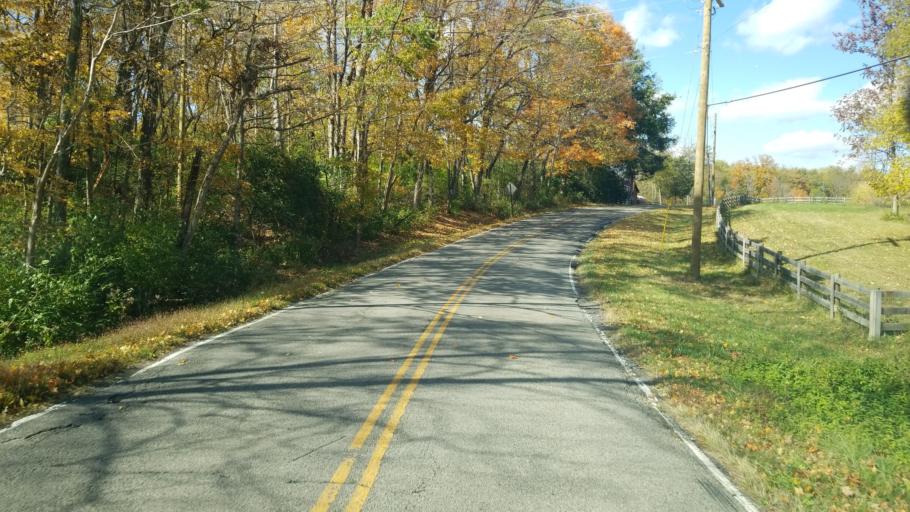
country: US
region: Ohio
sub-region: Warren County
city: Morrow
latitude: 39.4199
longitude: -84.0844
